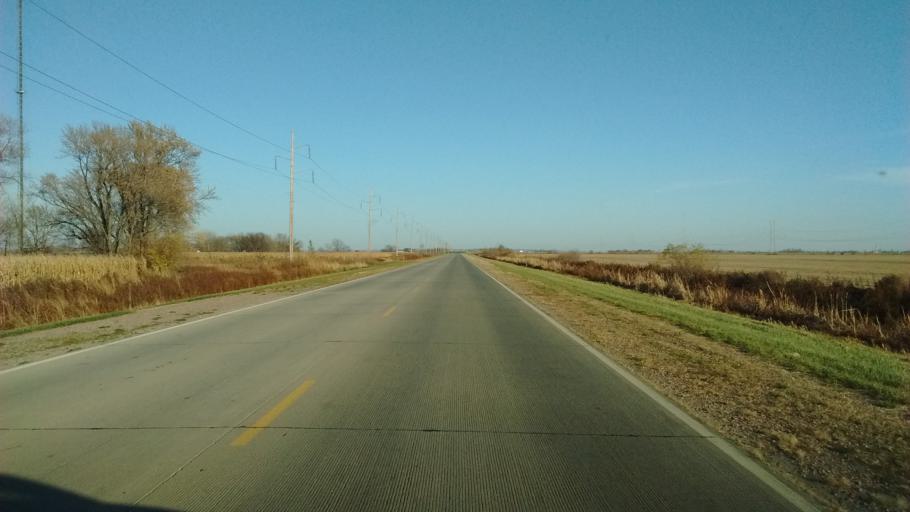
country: US
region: Iowa
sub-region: Woodbury County
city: Sergeant Bluff
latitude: 42.3302
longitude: -96.3388
